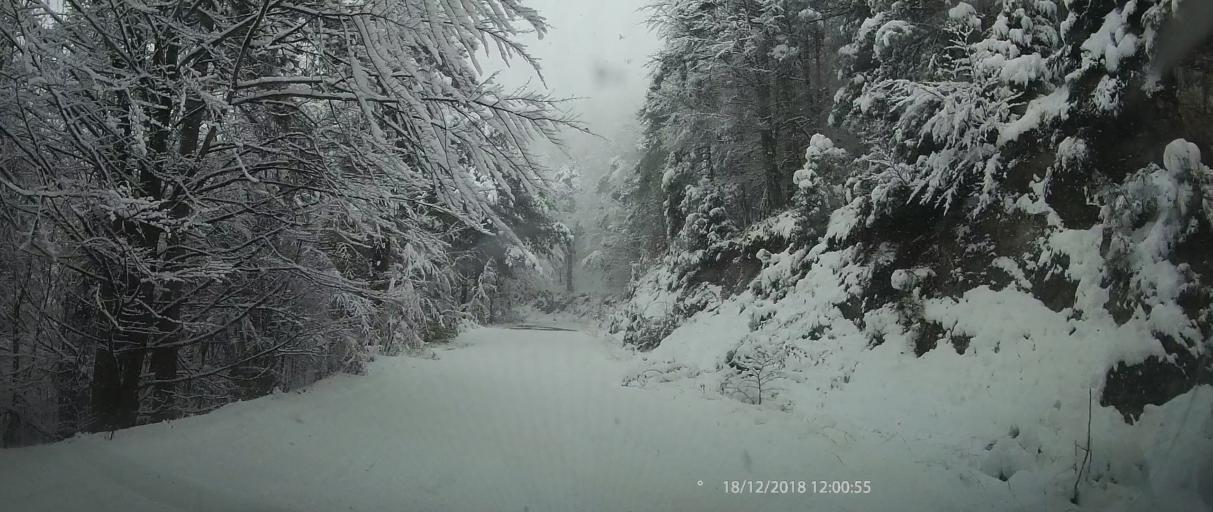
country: GR
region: Central Macedonia
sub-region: Nomos Pierias
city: Litochoro
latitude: 40.1097
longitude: 22.4627
